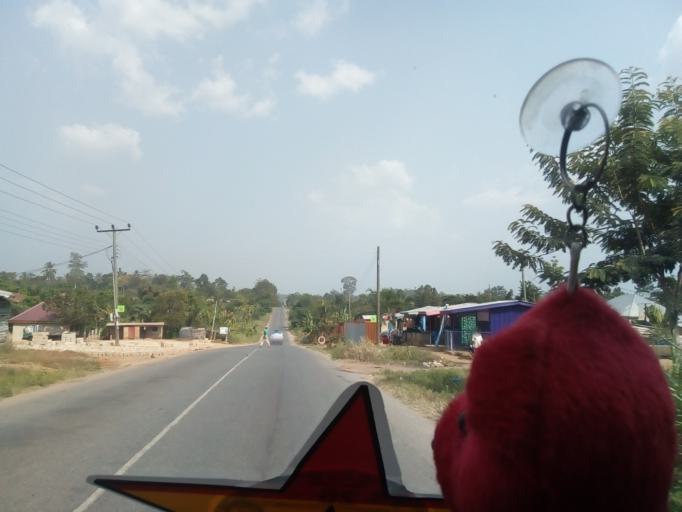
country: GH
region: Eastern
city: Suhum
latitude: 6.0430
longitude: -0.4317
